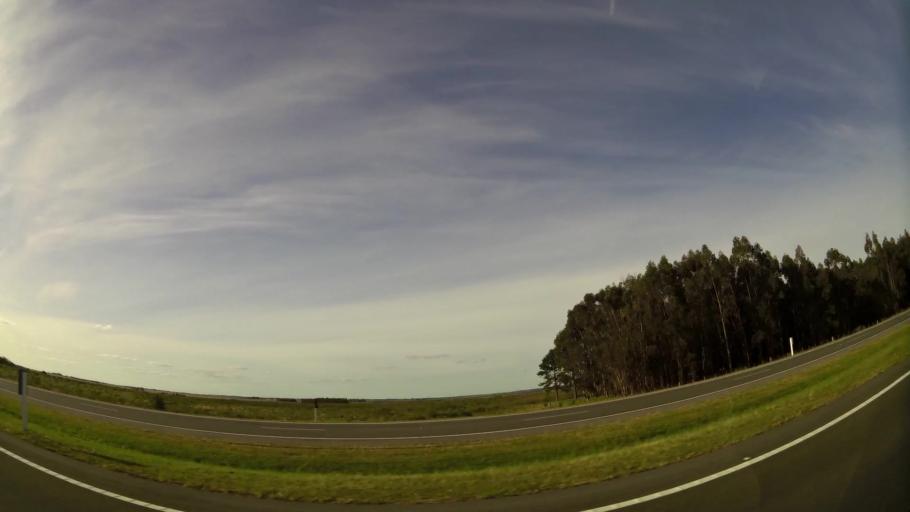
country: UY
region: Lavalleja
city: Solis de Mataojo
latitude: -34.7777
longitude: -55.4589
